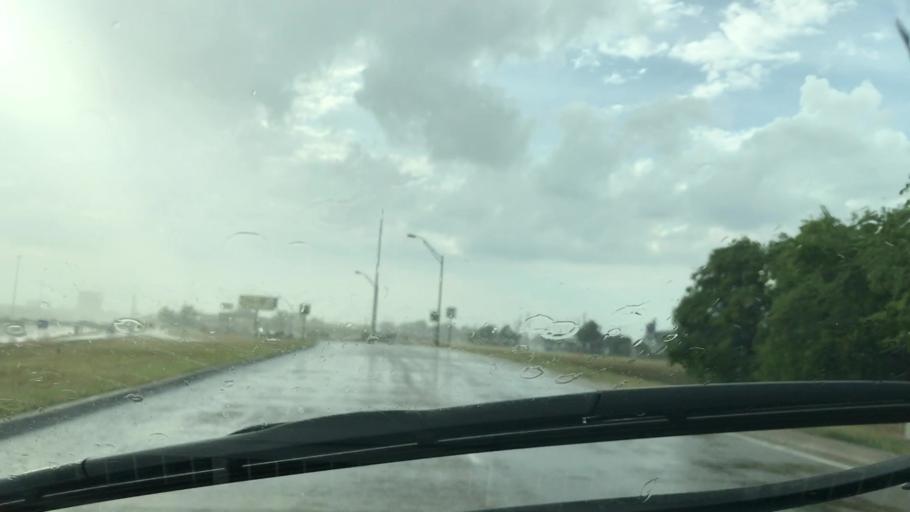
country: US
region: Texas
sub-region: Dallas County
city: Richardson
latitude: 32.8987
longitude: -96.7140
